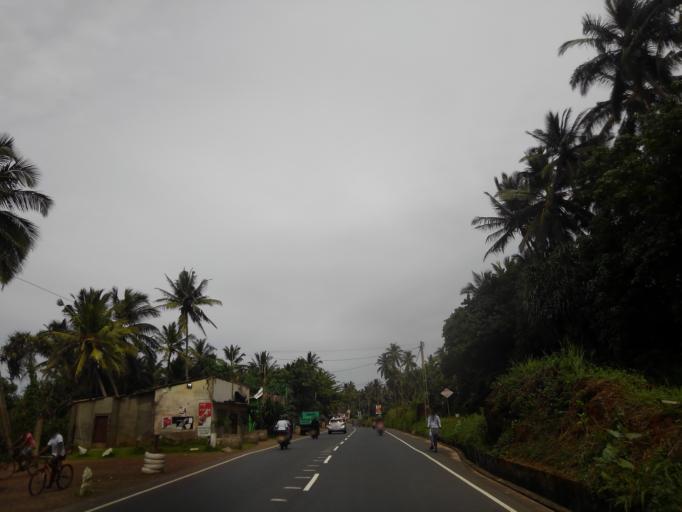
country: LK
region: Western
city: Beruwala
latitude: 6.4937
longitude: 79.9817
